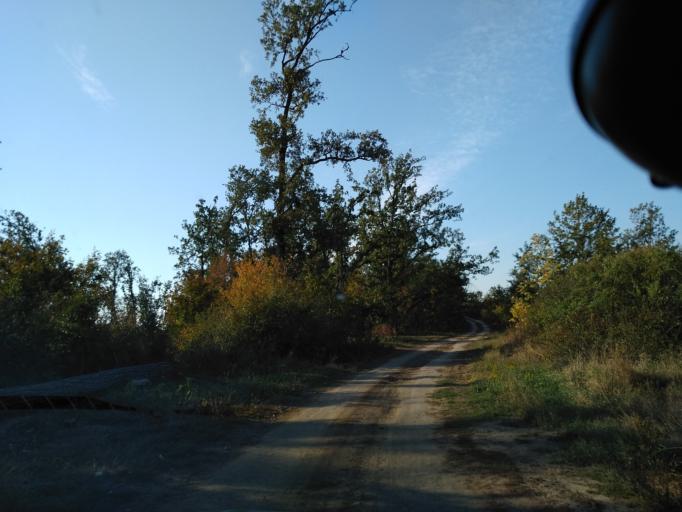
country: RO
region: Timis
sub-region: Comuna Bogda
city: Bogda
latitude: 45.9219
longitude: 21.6133
